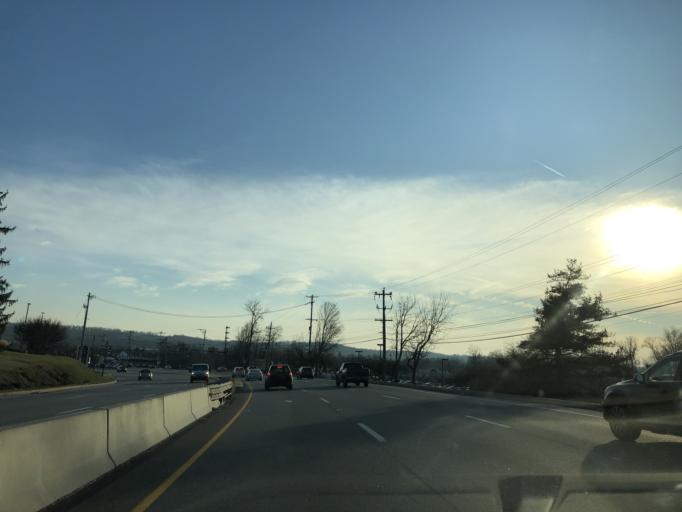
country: US
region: Pennsylvania
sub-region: Chester County
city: Exton
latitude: 40.0358
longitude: -75.6323
